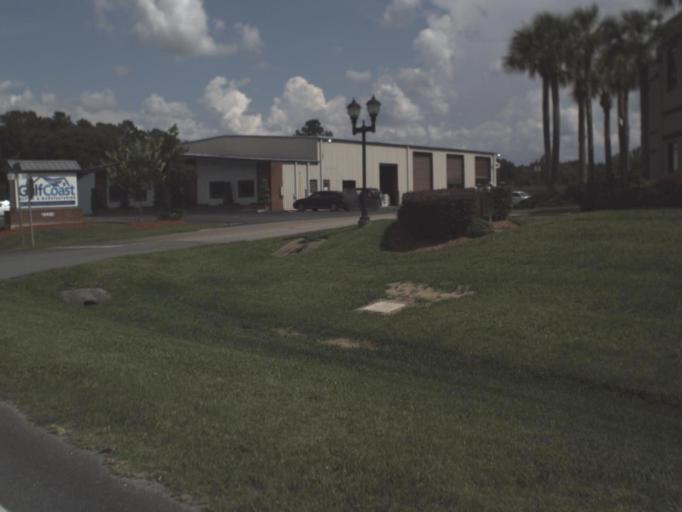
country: US
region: Florida
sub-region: Alachua County
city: Alachua
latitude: 29.7911
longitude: -82.4825
